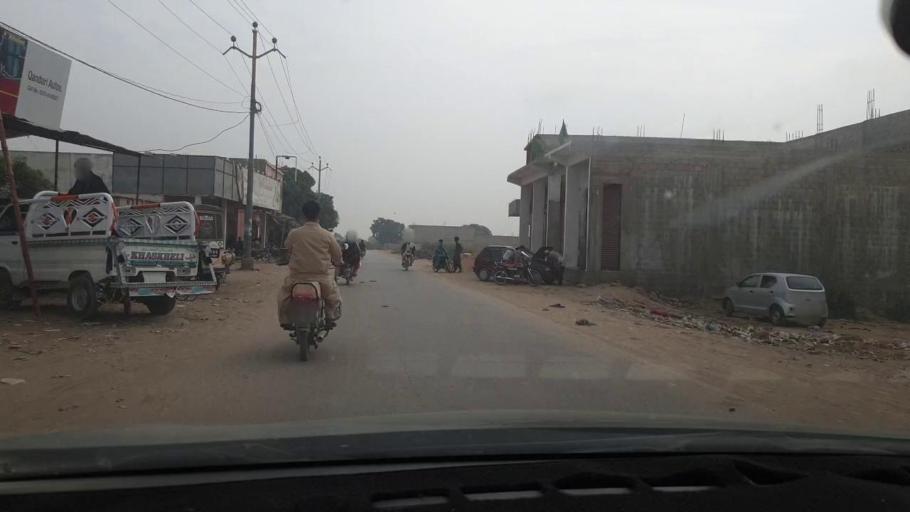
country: PK
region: Sindh
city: Malir Cantonment
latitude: 24.9190
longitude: 67.2583
